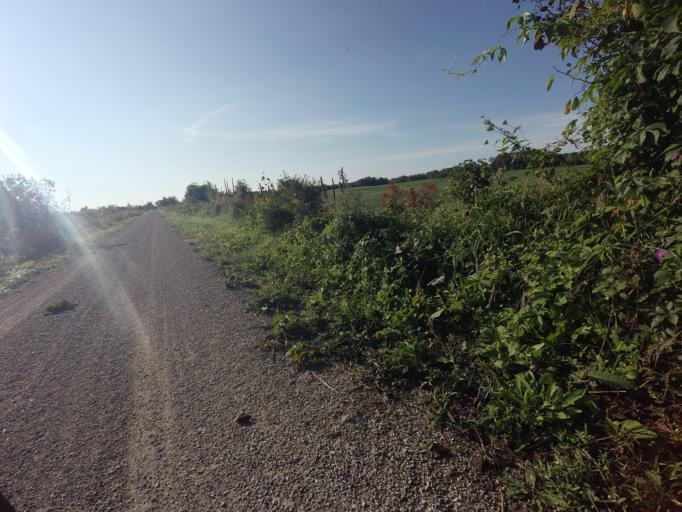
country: CA
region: Ontario
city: Goderich
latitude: 43.7566
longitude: -81.5147
